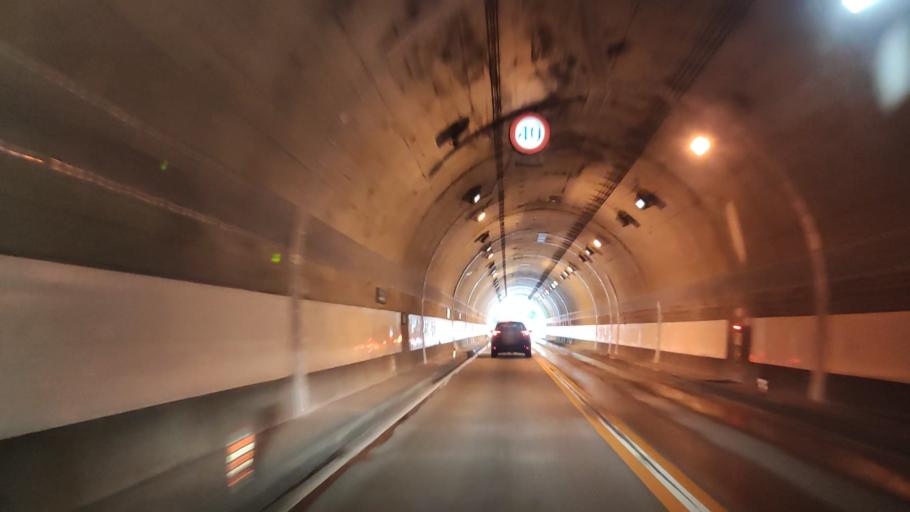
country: JP
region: Tokushima
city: Kamojimacho-jogejima
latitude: 34.1659
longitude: 134.3323
